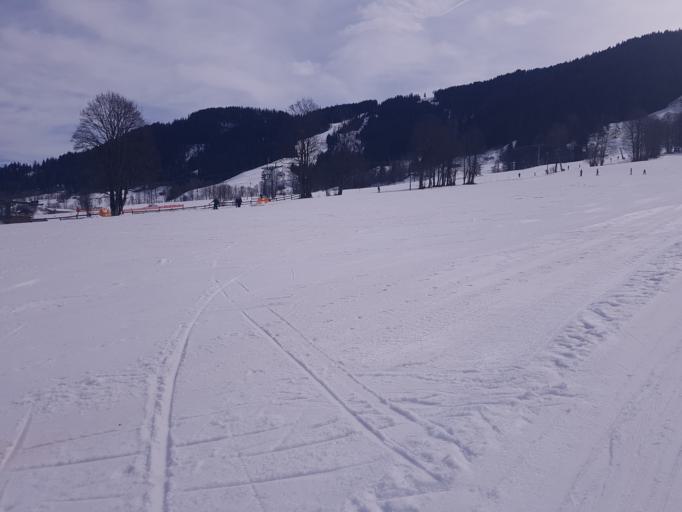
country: AT
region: Tyrol
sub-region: Politischer Bezirk Kufstein
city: Worgl
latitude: 47.4476
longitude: 12.0906
